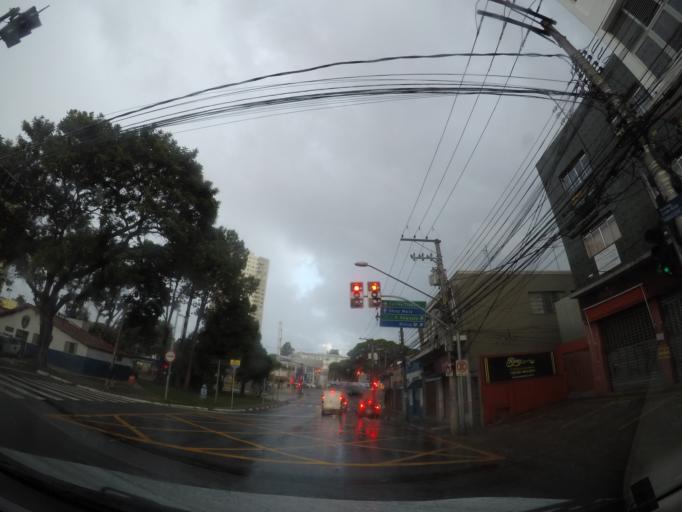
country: BR
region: Sao Paulo
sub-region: Guarulhos
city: Guarulhos
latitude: -23.4660
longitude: -46.5472
